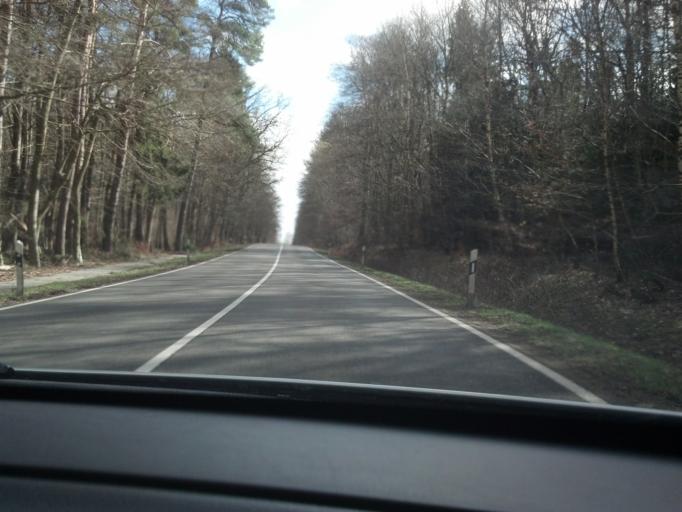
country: DE
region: Mecklenburg-Vorpommern
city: Zarrentin
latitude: 53.5033
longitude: 10.8621
